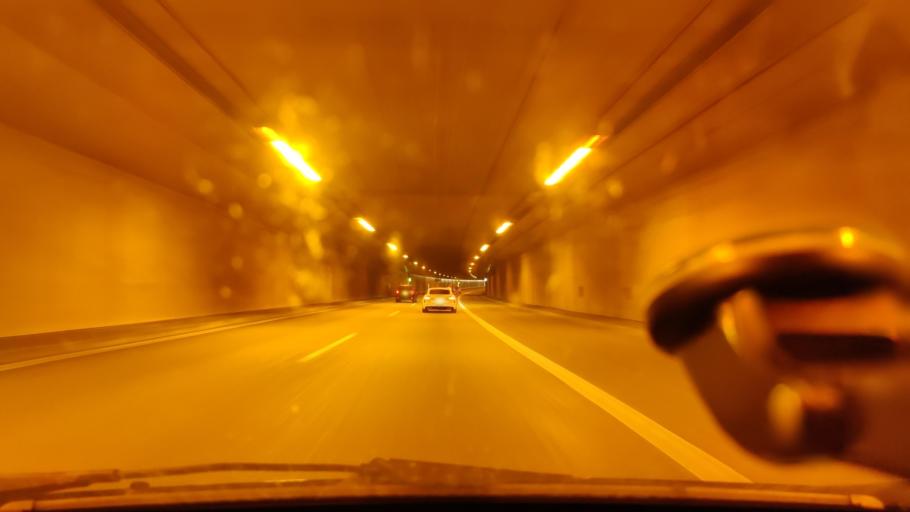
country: DE
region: North Rhine-Westphalia
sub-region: Regierungsbezirk Dusseldorf
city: Ratingen
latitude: 51.2739
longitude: 6.8336
